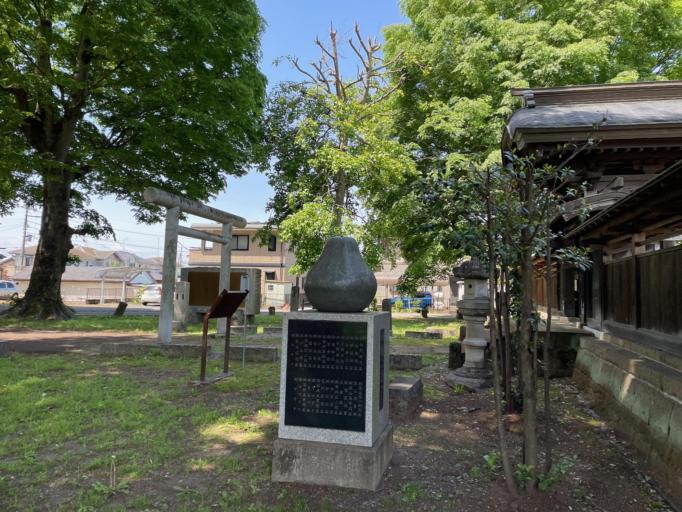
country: JP
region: Tochigi
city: Mibu
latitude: 36.4285
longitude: 139.7971
